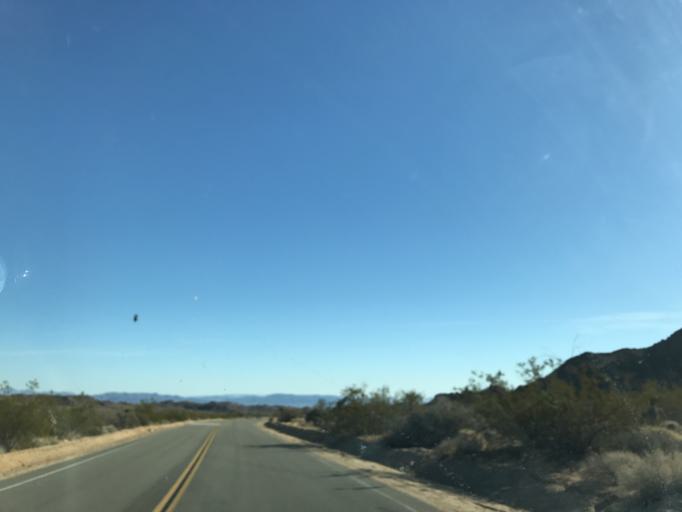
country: US
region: California
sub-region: Riverside County
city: Mecca
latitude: 33.7866
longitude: -115.7941
